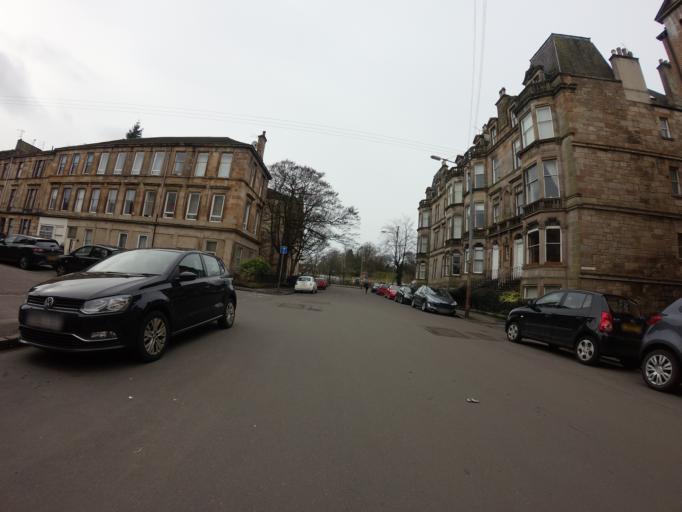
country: GB
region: Scotland
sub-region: Glasgow City
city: Glasgow
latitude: 55.8335
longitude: -4.2637
